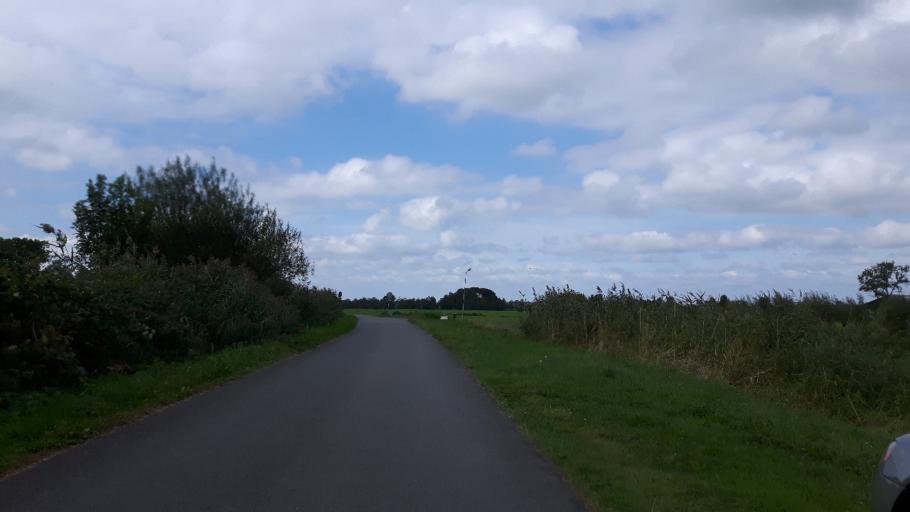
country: NL
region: Utrecht
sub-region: Gemeente De Ronde Venen
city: Mijdrecht
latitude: 52.1621
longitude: 4.9072
